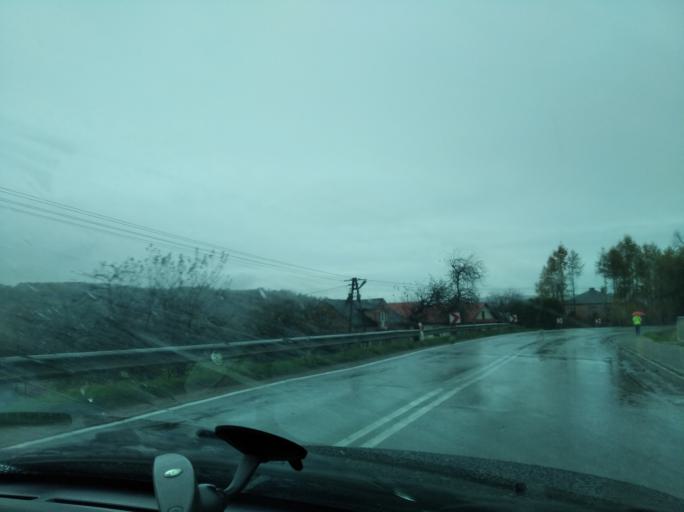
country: PL
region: Subcarpathian Voivodeship
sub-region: Powiat rzeszowski
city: Chmielnik
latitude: 49.9455
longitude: 22.1011
